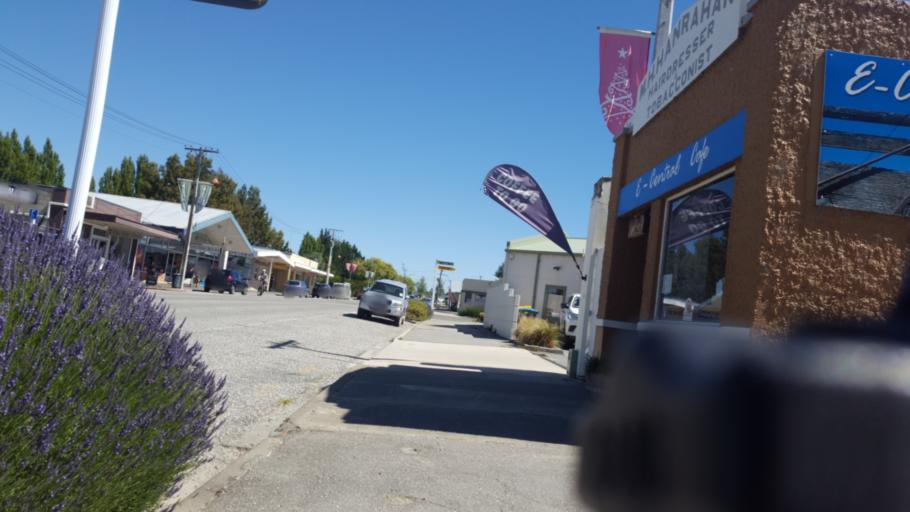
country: NZ
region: Otago
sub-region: Dunedin City
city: Dunedin
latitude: -45.1296
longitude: 170.0991
